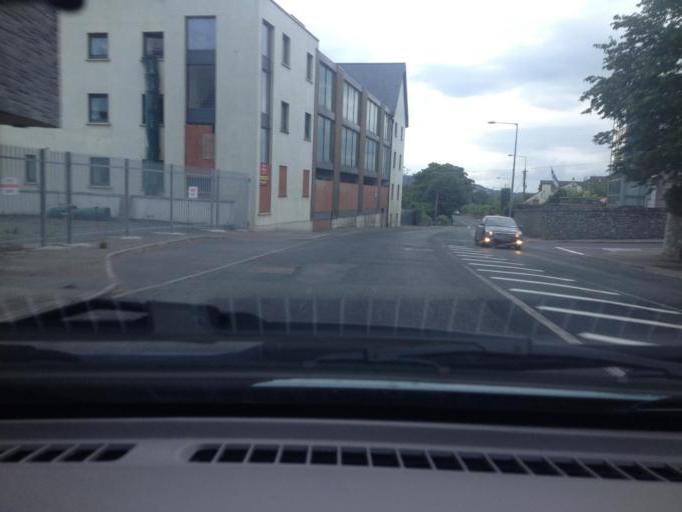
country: IE
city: Ballisodare
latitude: 54.2120
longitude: -8.5089
